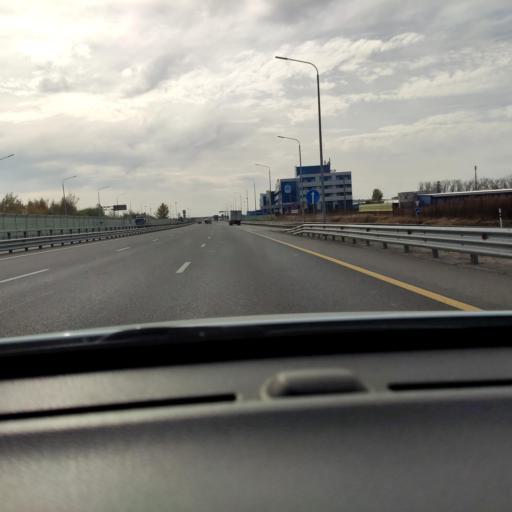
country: RU
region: Voronezj
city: Somovo
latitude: 51.6839
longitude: 39.3025
